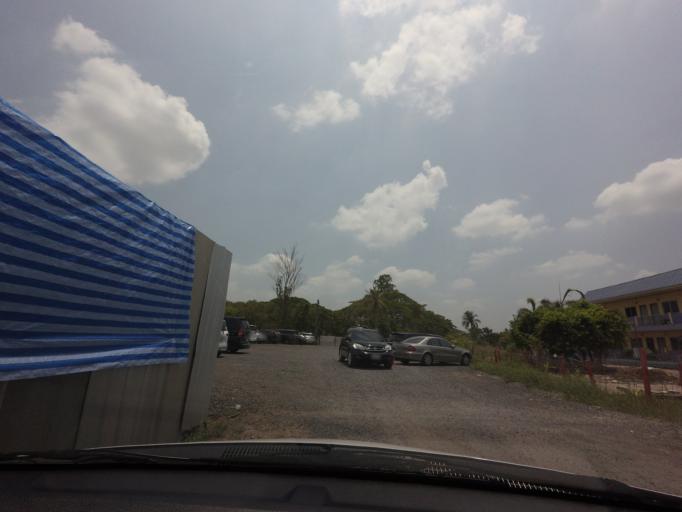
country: TH
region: Pathum Thani
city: Sam Khok
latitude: 14.0455
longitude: 100.5517
